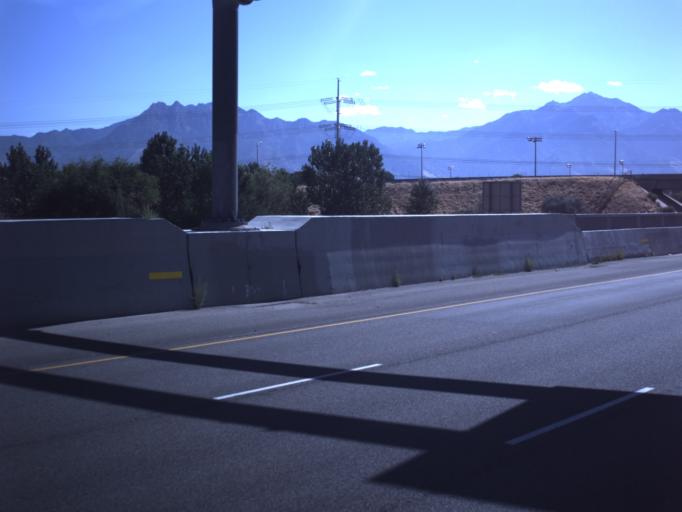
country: US
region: Utah
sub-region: Salt Lake County
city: Taylorsville
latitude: 40.6390
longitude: -111.9226
